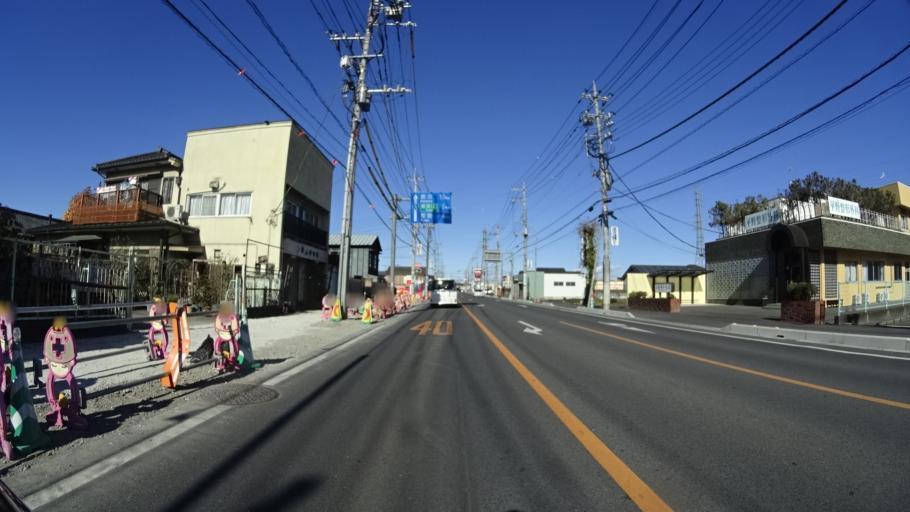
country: JP
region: Tochigi
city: Tochigi
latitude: 36.3950
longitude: 139.7372
